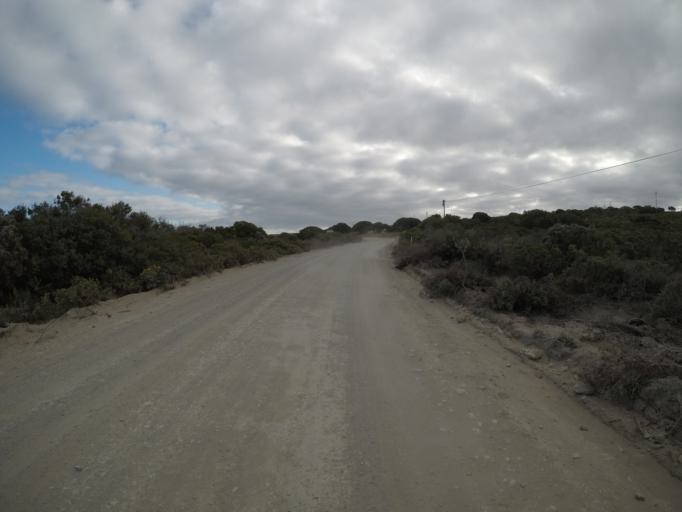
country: ZA
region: Western Cape
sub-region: Eden District Municipality
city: Riversdale
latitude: -34.4209
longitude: 21.3328
